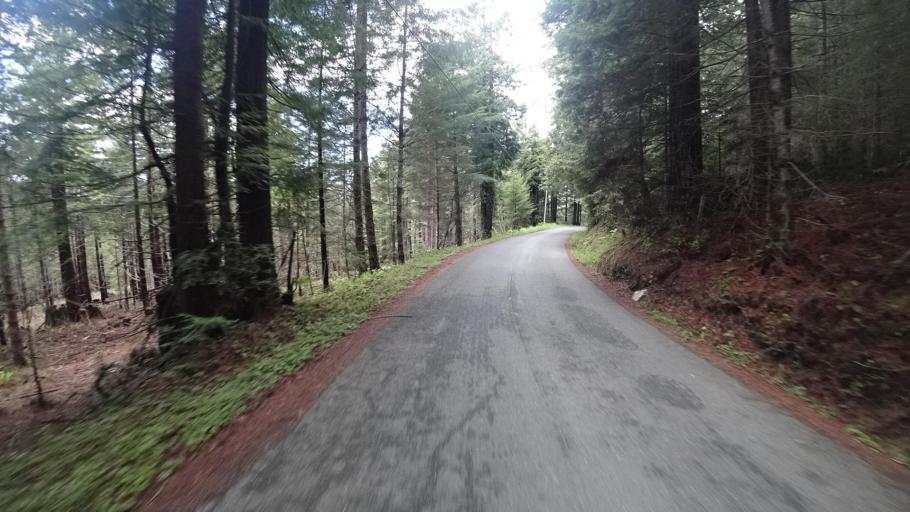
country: US
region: California
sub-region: Humboldt County
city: Blue Lake
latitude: 40.8516
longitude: -123.9289
